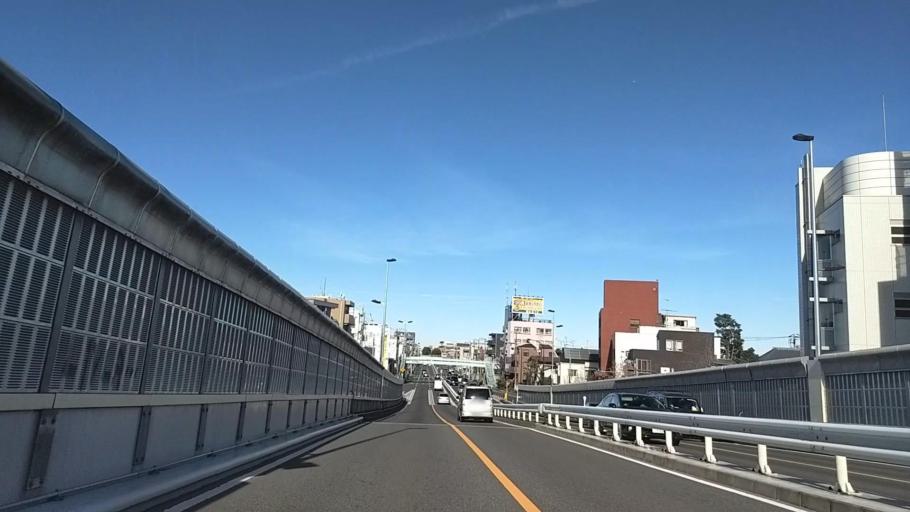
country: JP
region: Kanagawa
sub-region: Kawasaki-shi
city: Kawasaki
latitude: 35.5899
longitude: 139.6772
